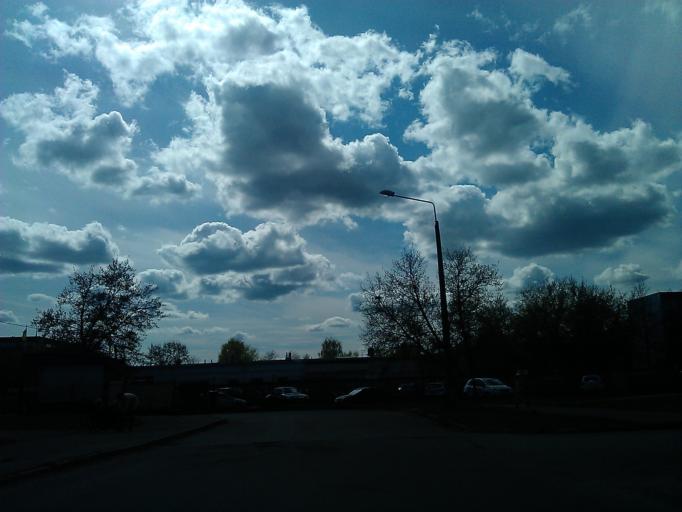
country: LV
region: Kekava
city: Balozi
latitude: 56.9073
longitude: 24.1904
